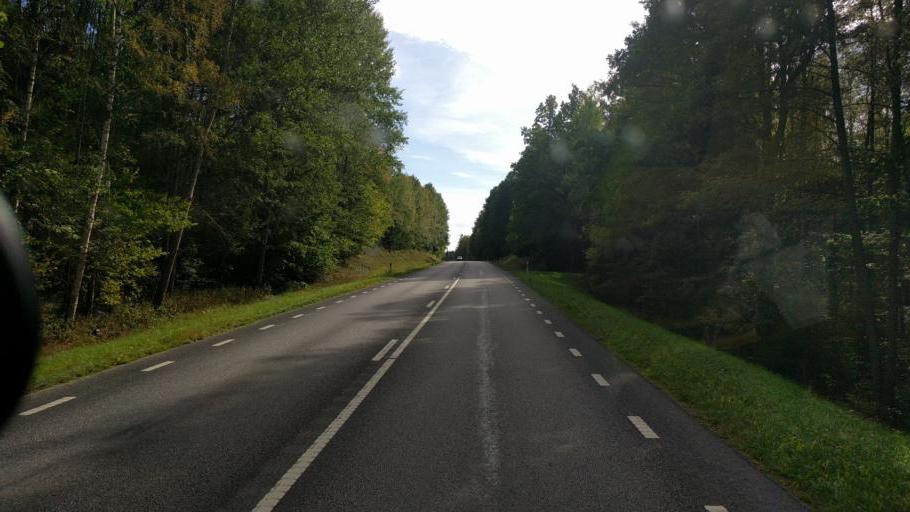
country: SE
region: OEstergoetland
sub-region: Kinda Kommun
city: Kisa
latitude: 57.9398
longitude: 15.6674
